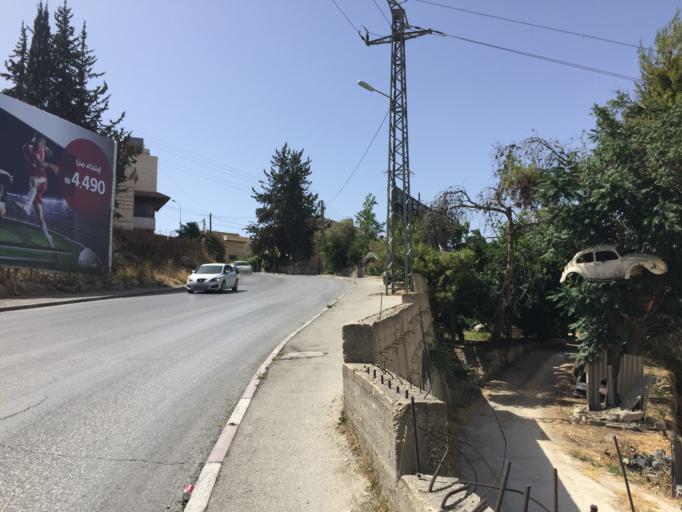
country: PS
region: West Bank
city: Bethlehem
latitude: 31.7048
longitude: 35.2126
